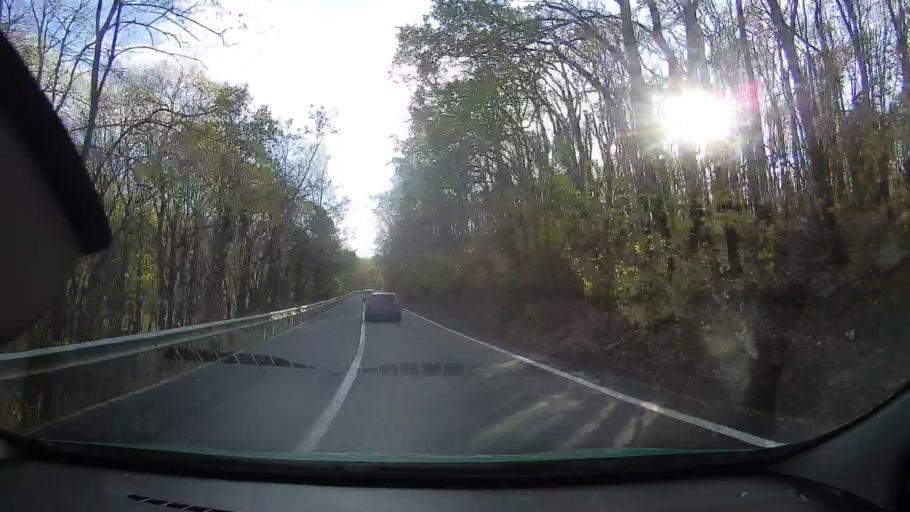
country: RO
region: Tulcea
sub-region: Comuna Topolog
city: Topolog
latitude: 44.9130
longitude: 28.4193
